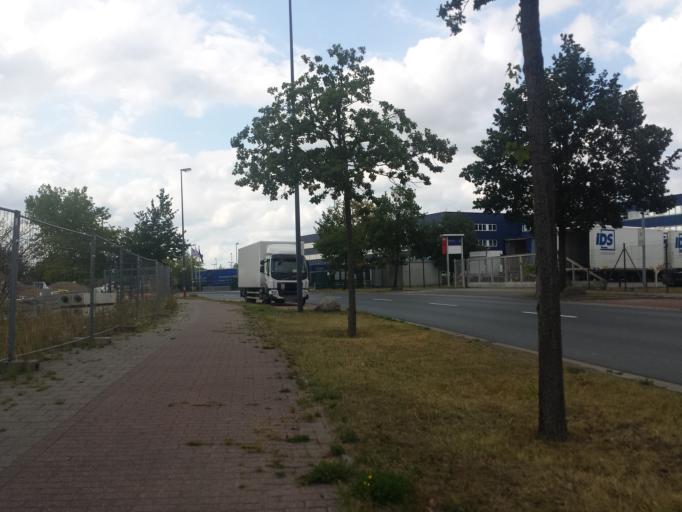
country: DE
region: Lower Saxony
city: Stuhr
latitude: 53.0892
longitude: 8.7074
